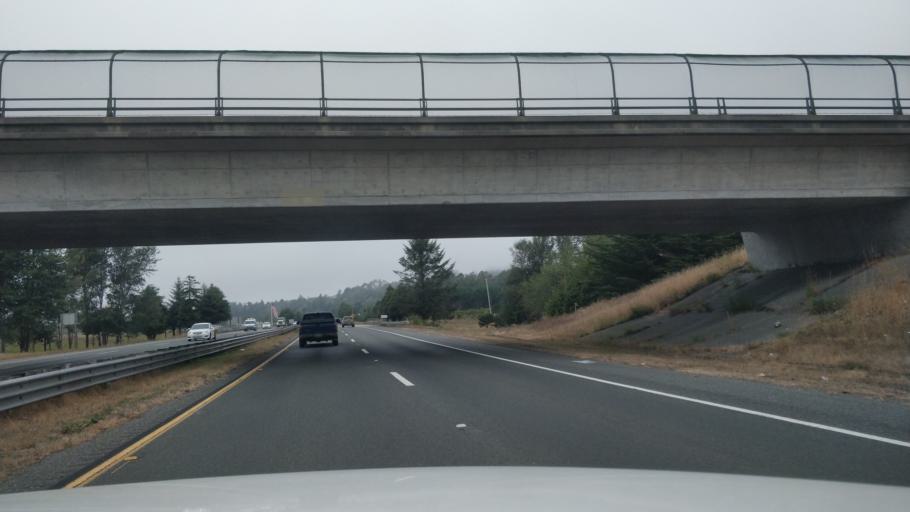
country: US
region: California
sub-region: Humboldt County
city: Arcata
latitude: 40.9041
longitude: -124.0866
